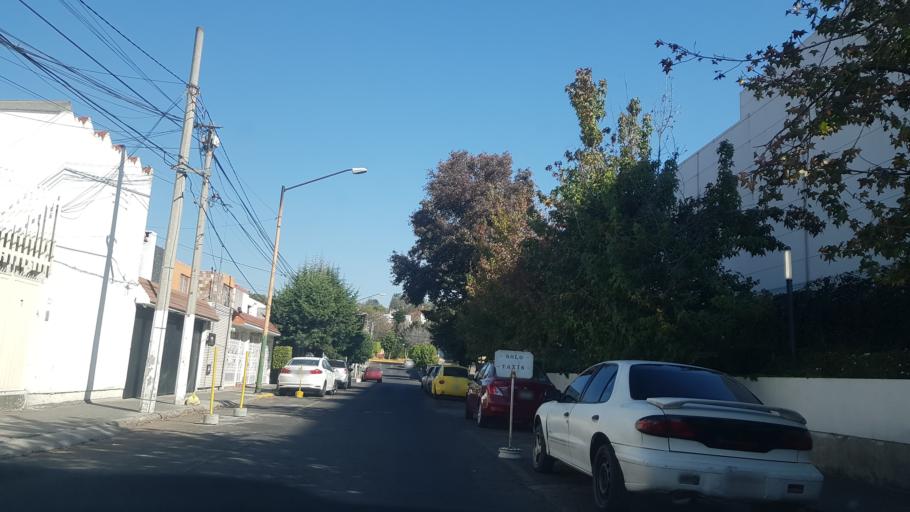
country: MX
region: Mexico
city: Naucalpan de Juarez
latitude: 19.4961
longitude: -99.2478
